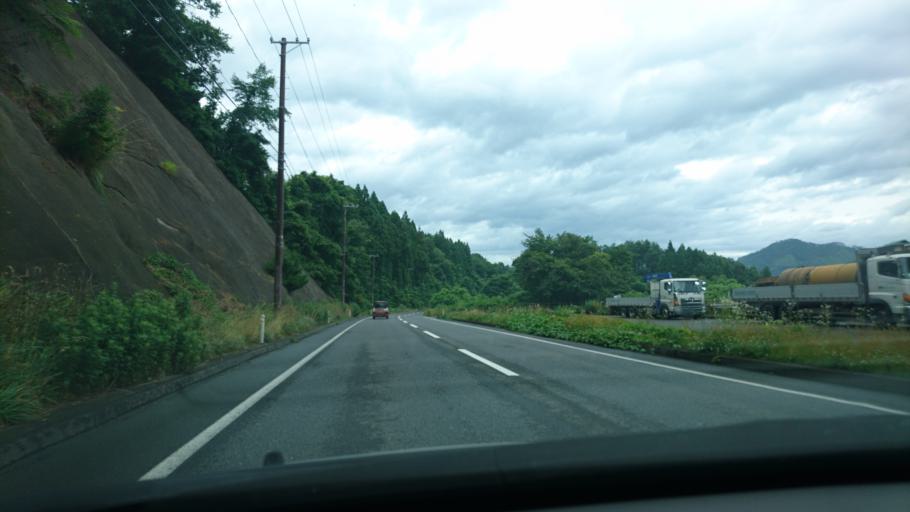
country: JP
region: Iwate
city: Yamada
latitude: 39.4122
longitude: 141.9624
